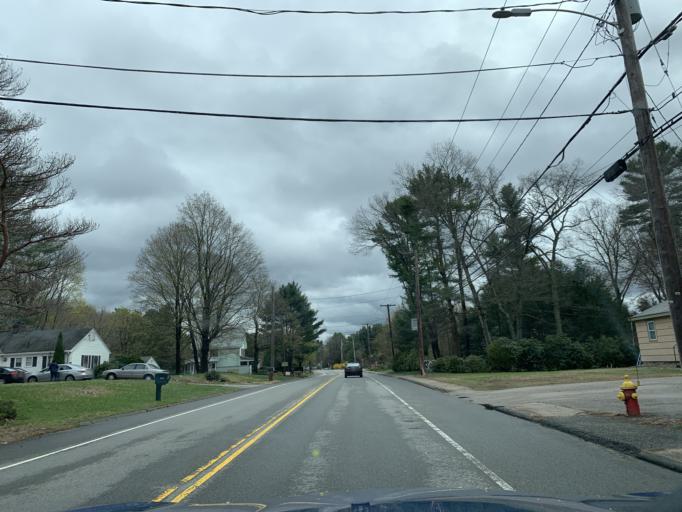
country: US
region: Massachusetts
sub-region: Bristol County
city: Mansfield Center
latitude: 41.9894
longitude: -71.2422
